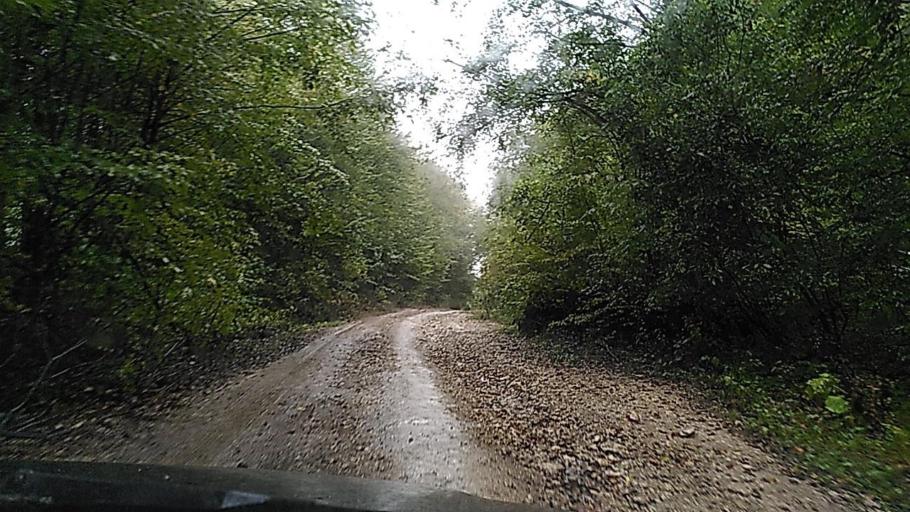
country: RU
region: Kabardino-Balkariya
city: Belaya Rechka
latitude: 43.3808
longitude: 43.4361
